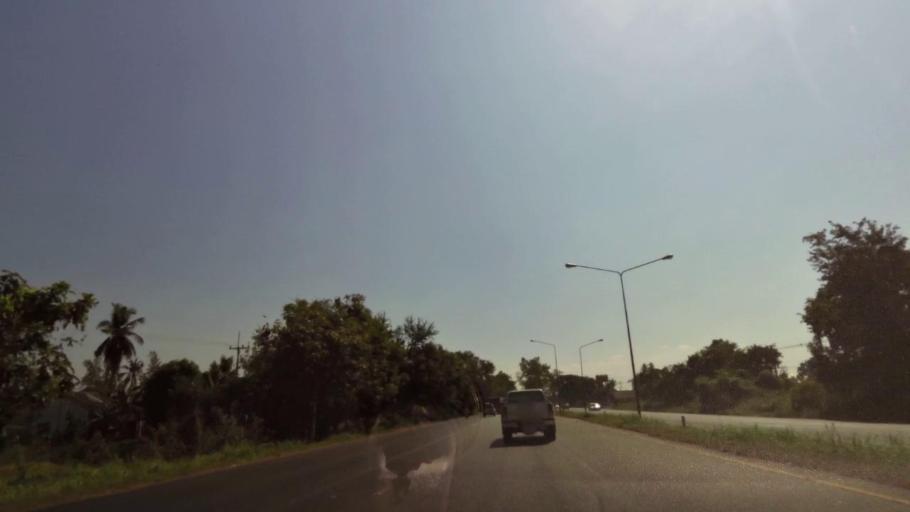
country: TH
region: Nakhon Sawan
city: Kao Liao
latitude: 15.8245
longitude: 100.1191
